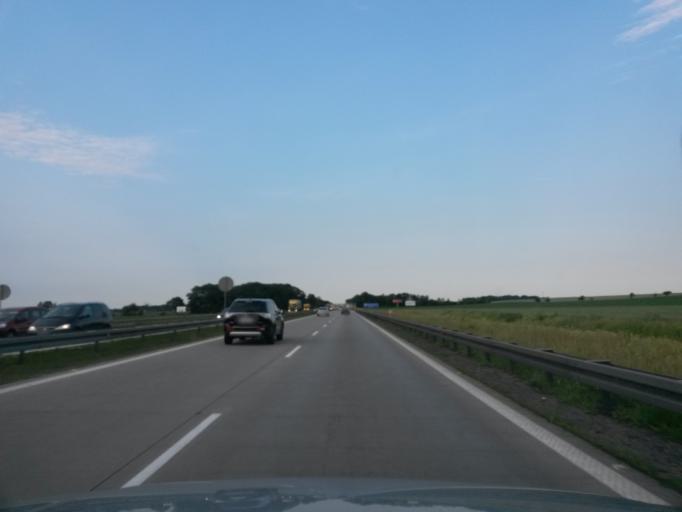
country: PL
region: Lower Silesian Voivodeship
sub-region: Powiat wroclawski
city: Gniechowice
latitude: 51.0349
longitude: 16.8439
